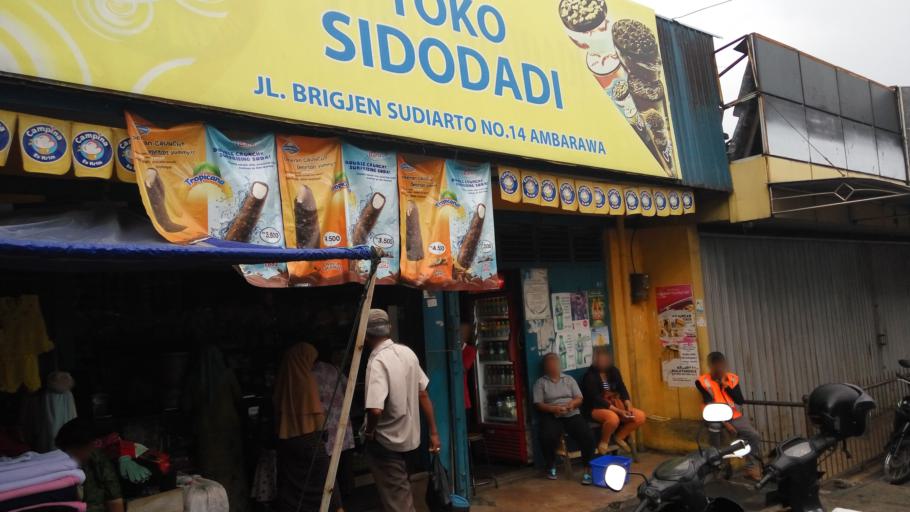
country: ID
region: Central Java
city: Ambarawa
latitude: -7.2579
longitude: 110.4059
